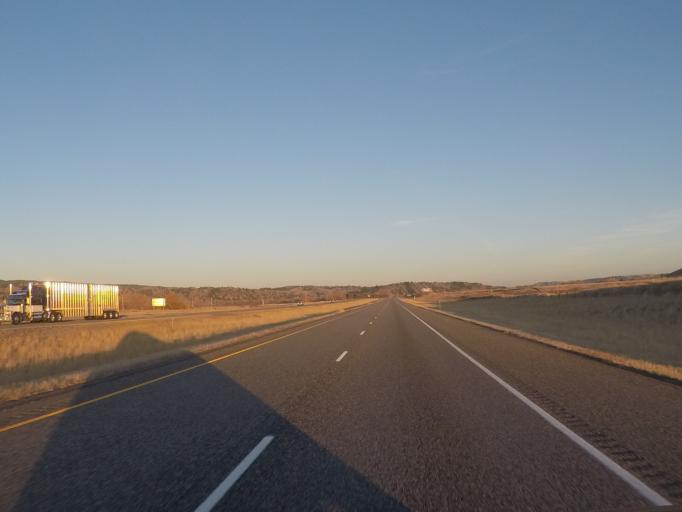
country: US
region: Montana
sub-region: Sweet Grass County
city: Big Timber
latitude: 45.7335
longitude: -109.6991
